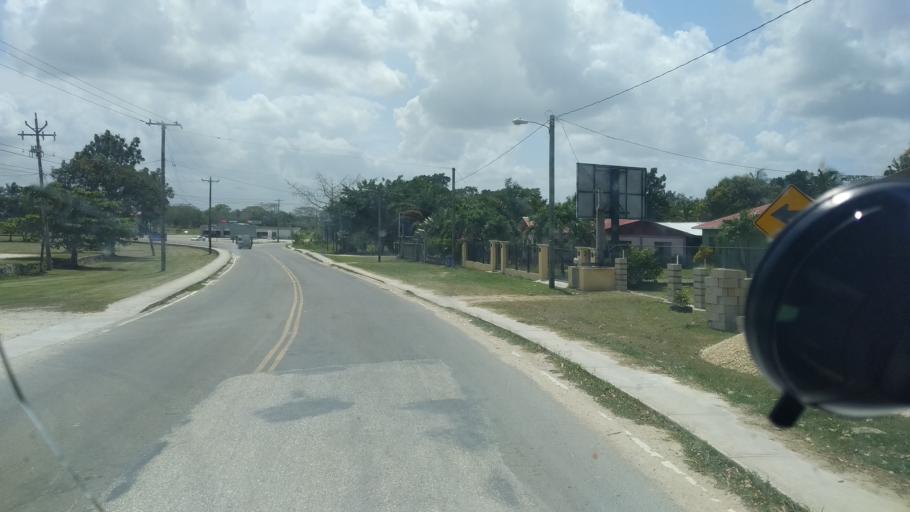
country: BZ
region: Orange Walk
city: Orange Walk
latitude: 18.0637
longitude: -88.5722
